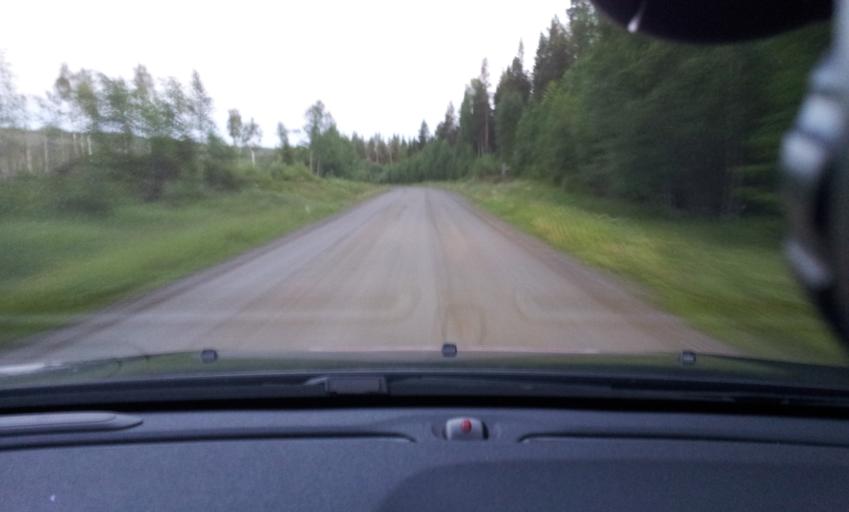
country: SE
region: Jaemtland
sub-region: Ragunda Kommun
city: Hammarstrand
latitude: 62.8770
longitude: 16.0587
